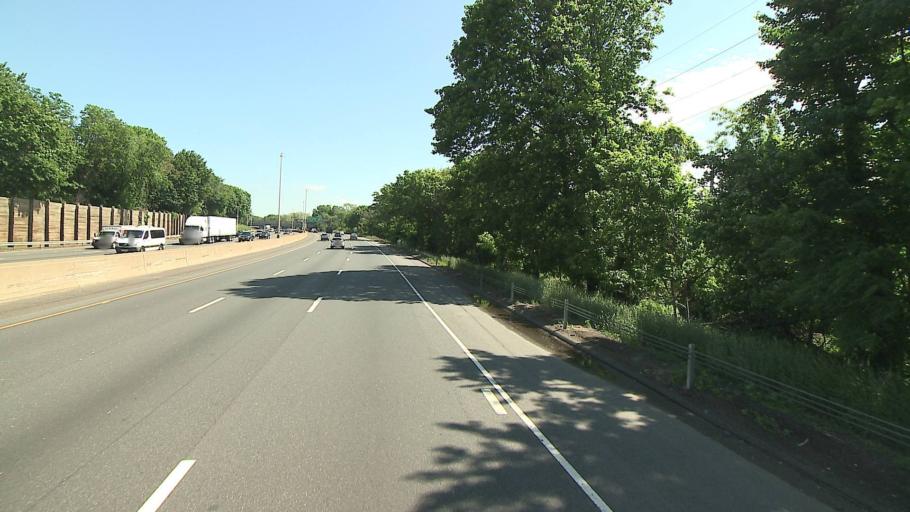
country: US
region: Connecticut
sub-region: Fairfield County
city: Fairfield
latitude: 41.1517
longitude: -73.2470
